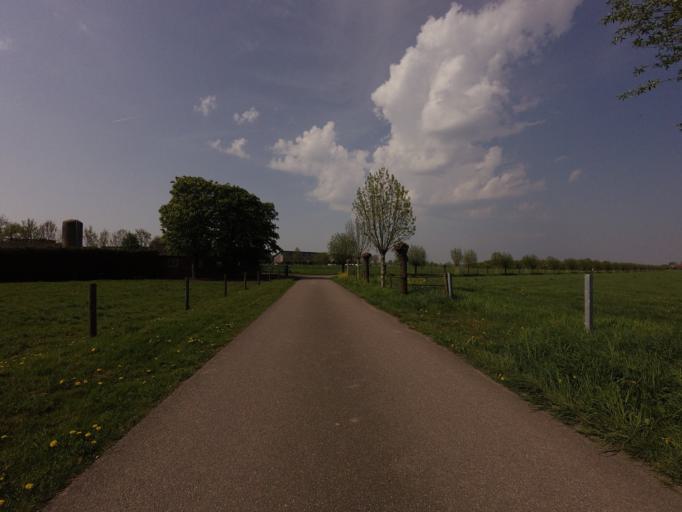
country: NL
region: Utrecht
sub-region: Gemeente Houten
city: Houten
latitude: 52.0185
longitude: 5.1997
